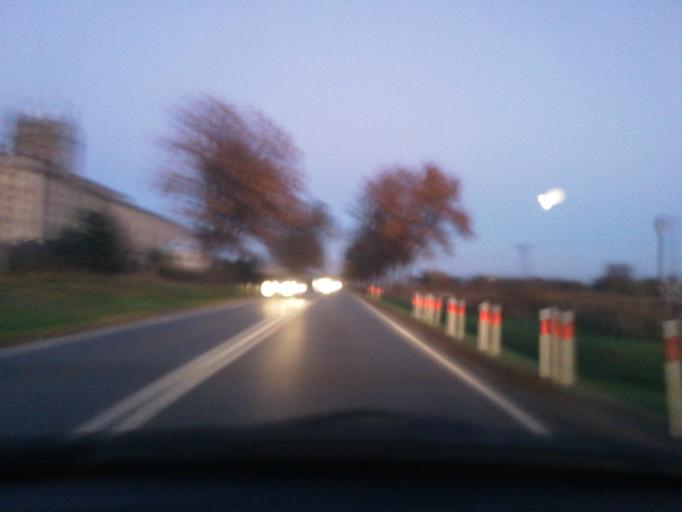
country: PL
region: Lodz Voivodeship
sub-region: Powiat brzezinski
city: Rogow
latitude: 51.8065
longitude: 19.8779
